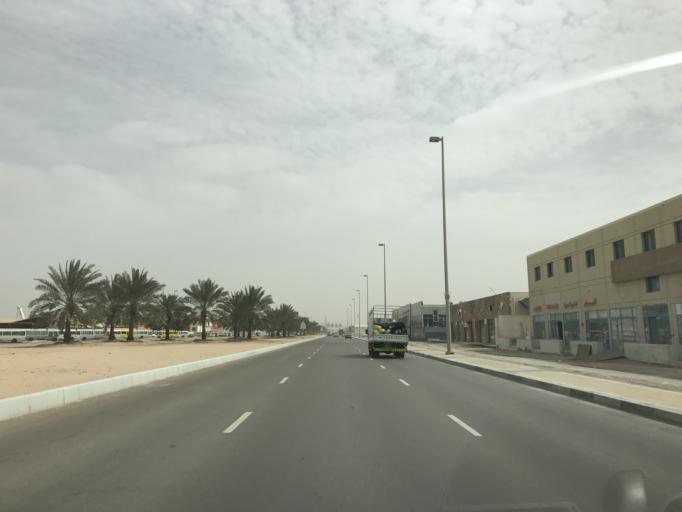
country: AE
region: Abu Dhabi
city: Abu Dhabi
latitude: 24.3722
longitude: 54.4874
